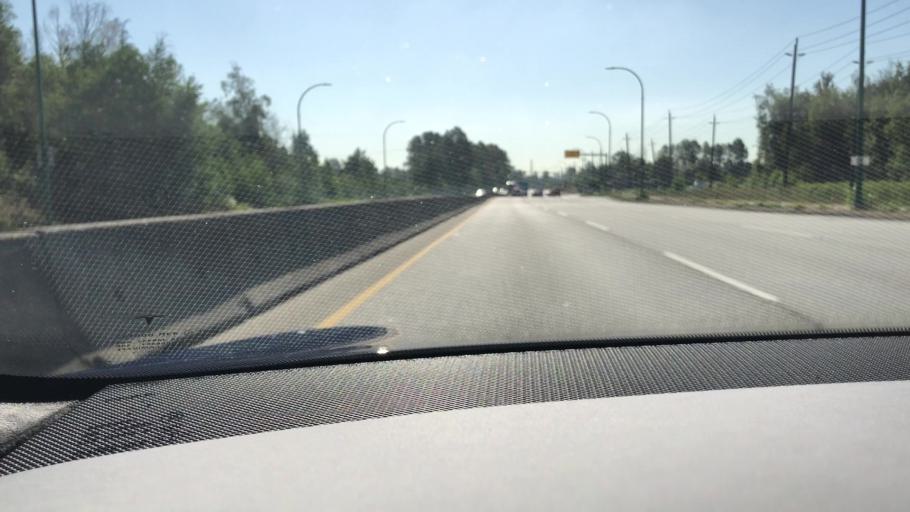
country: CA
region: British Columbia
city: New Westminster
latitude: 49.1971
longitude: -122.9721
